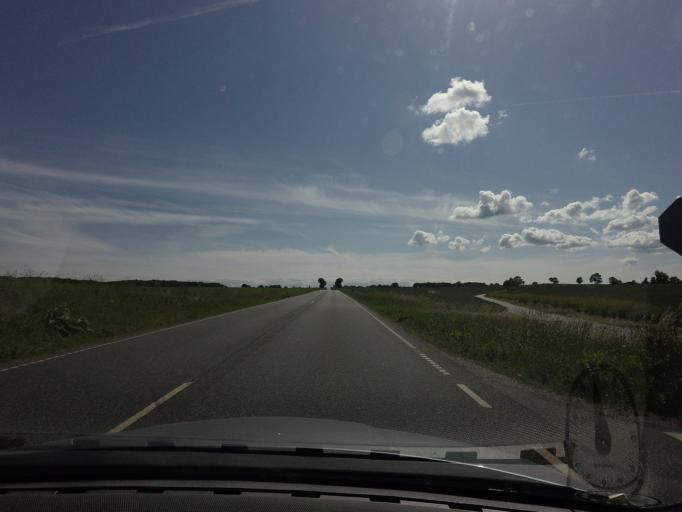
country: DK
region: Central Jutland
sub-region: Syddjurs Kommune
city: Ebeltoft
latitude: 56.3223
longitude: 10.7114
